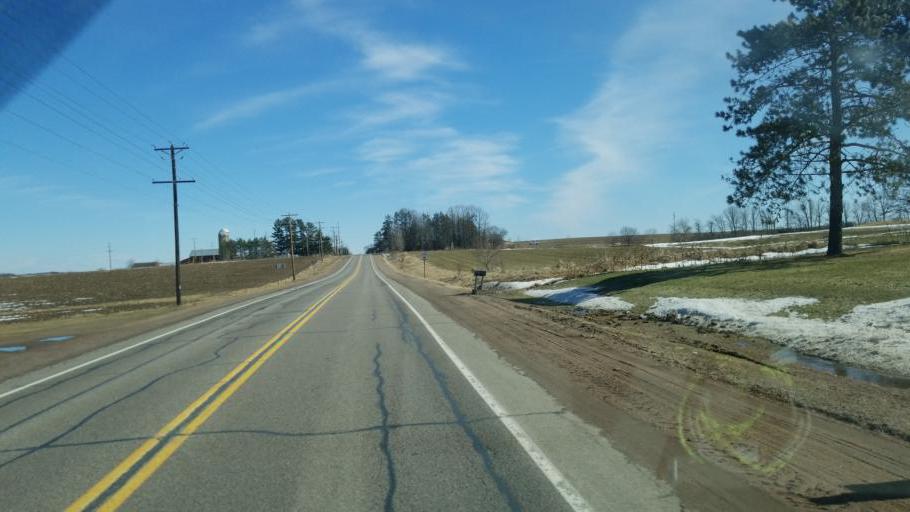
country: US
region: Wisconsin
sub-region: Clark County
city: Loyal
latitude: 44.5824
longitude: -90.4008
